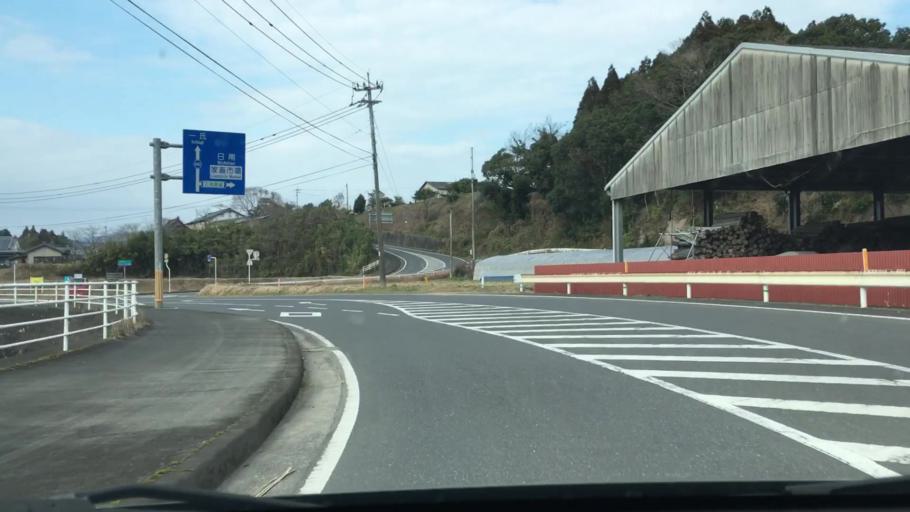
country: JP
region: Miyazaki
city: Kushima
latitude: 31.5002
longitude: 131.2389
